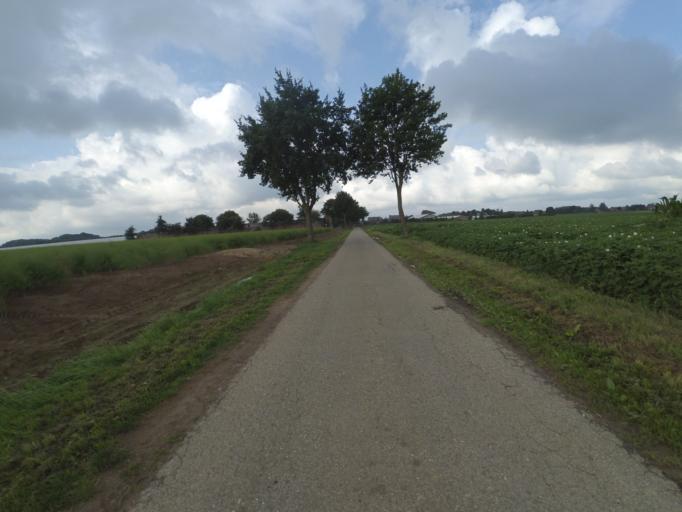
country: DE
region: North Rhine-Westphalia
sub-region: Regierungsbezirk Koln
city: Selfkant
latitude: 51.0411
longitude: 5.9167
